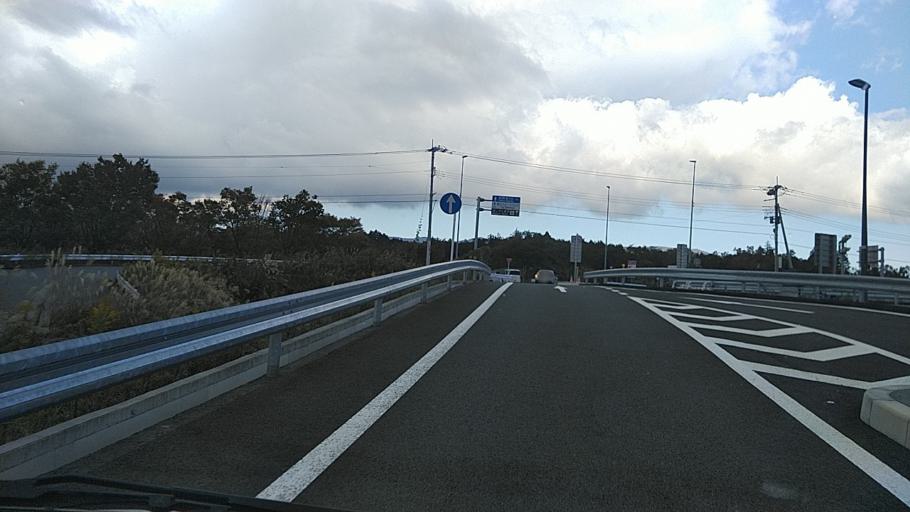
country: JP
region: Shizuoka
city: Gotemba
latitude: 35.3152
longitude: 138.9689
